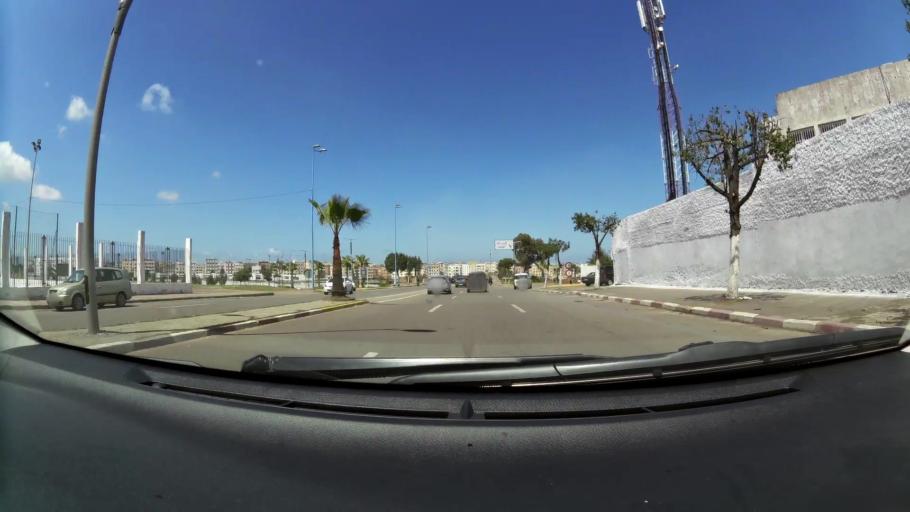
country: MA
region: Grand Casablanca
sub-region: Casablanca
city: Casablanca
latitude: 33.5596
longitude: -7.5876
